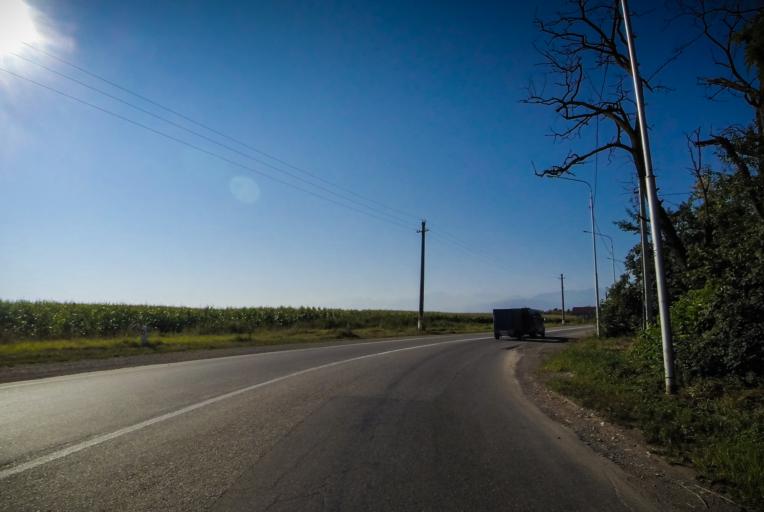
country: RU
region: North Ossetia
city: Arkhonskaya
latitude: 43.1187
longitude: 44.5240
